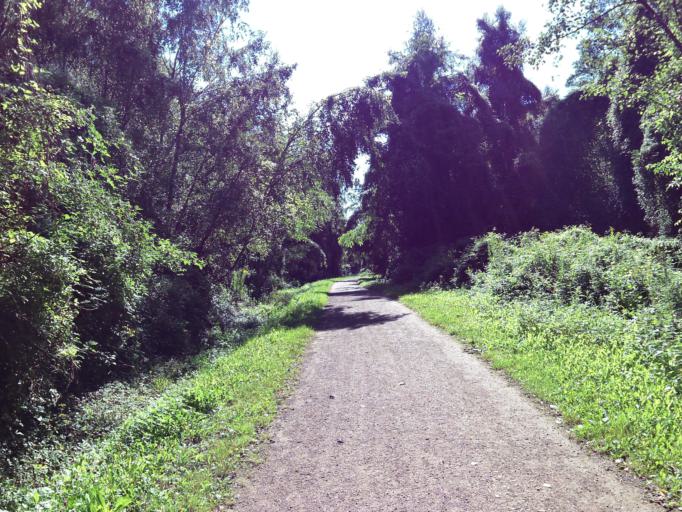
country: DE
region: North Rhine-Westphalia
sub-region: Regierungsbezirk Koln
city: Herzogenrath
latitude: 50.8907
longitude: 6.1061
